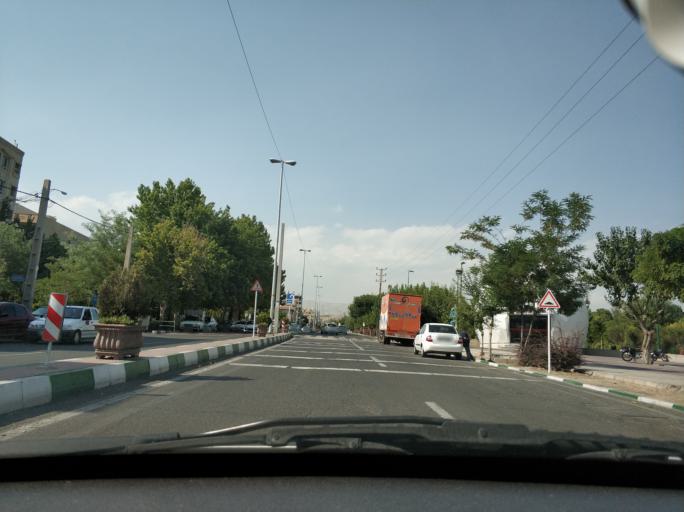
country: IR
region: Tehran
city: Tajrish
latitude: 35.7552
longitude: 51.5390
